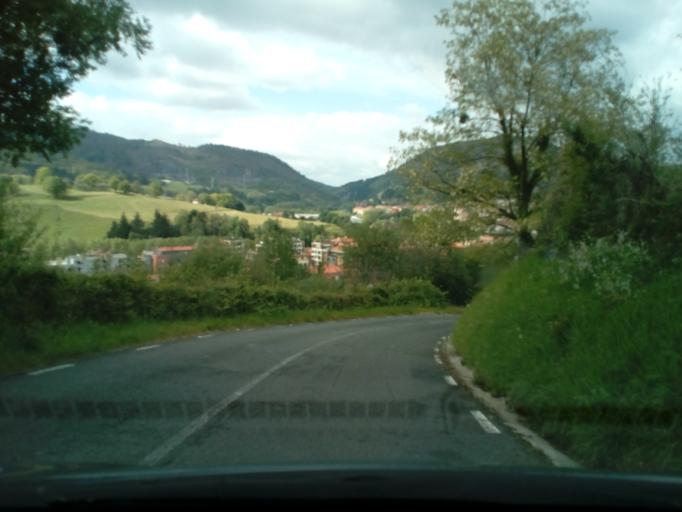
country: ES
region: Basque Country
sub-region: Provincia de Guipuzcoa
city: Andoain
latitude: 43.2094
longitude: -2.0241
